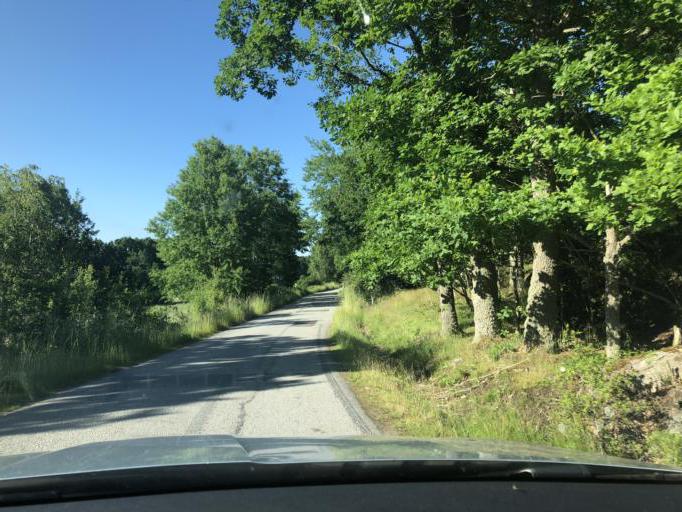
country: SE
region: Blekinge
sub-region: Karlshamns Kommun
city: Morrum
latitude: 56.1616
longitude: 14.8014
